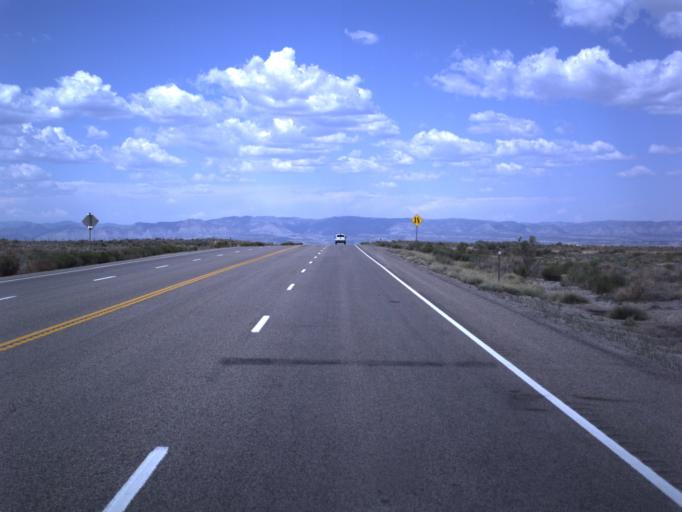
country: US
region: Utah
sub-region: Carbon County
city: Price
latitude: 39.4779
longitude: -110.8536
